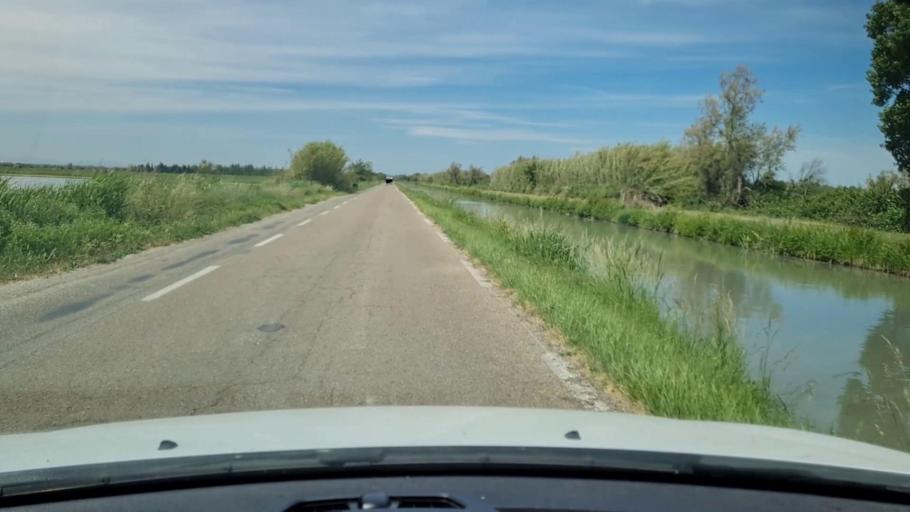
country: FR
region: Languedoc-Roussillon
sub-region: Departement du Gard
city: Saint-Gilles
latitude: 43.5925
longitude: 4.3431
